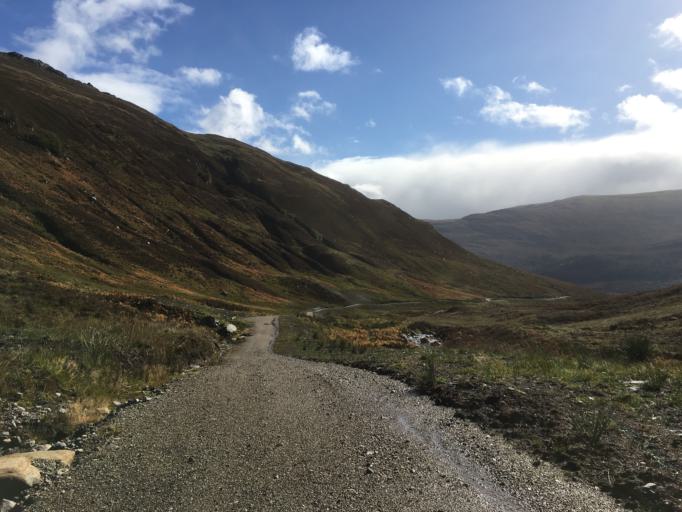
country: GB
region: Scotland
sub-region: Highland
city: Spean Bridge
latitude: 57.3521
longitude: -4.9878
